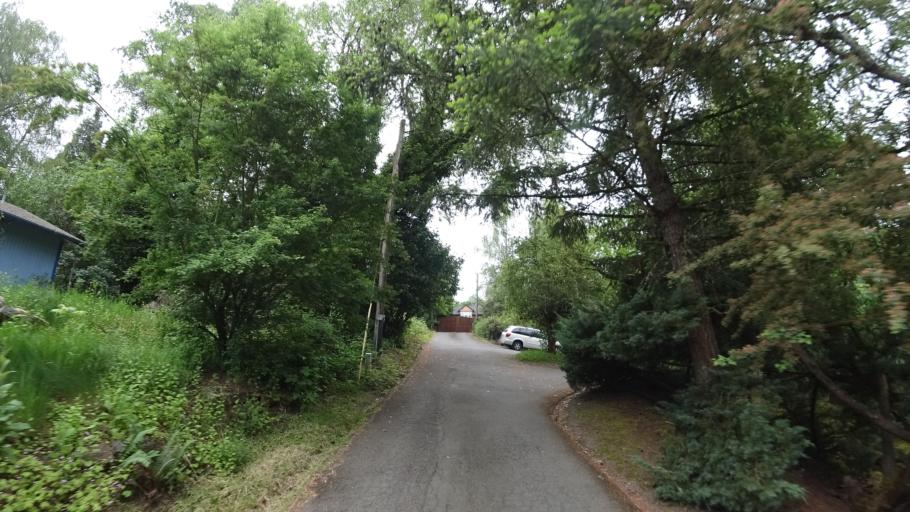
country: US
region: Oregon
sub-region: Washington County
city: Garden Home-Whitford
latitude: 45.4672
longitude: -122.7369
